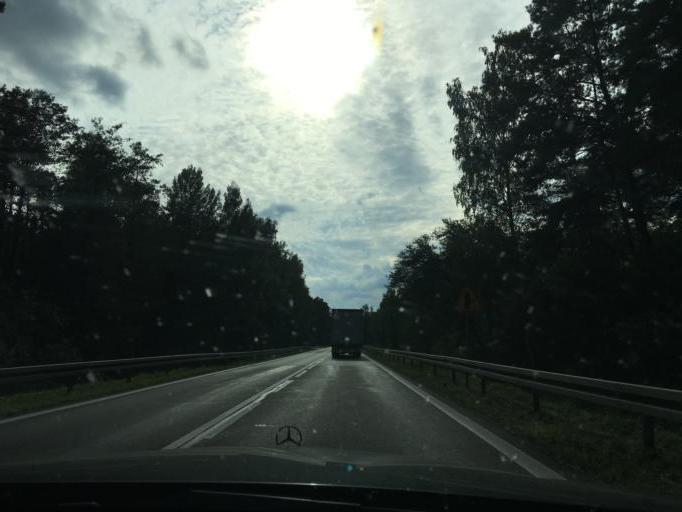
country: PL
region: Podlasie
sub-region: Powiat grajewski
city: Rajgrod
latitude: 53.6963
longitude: 22.6464
